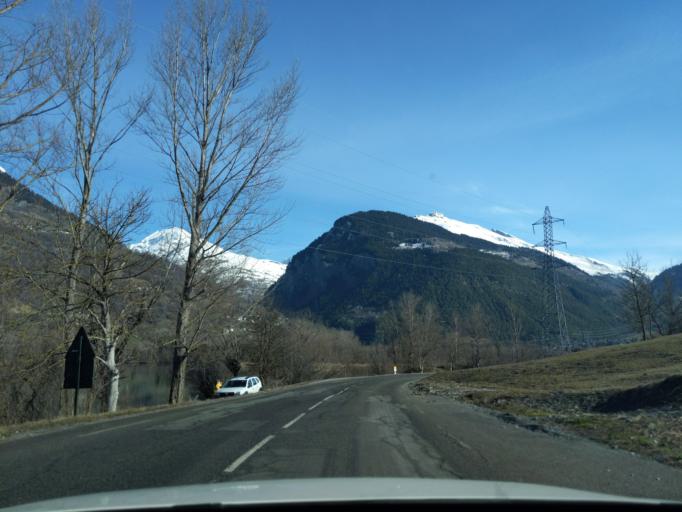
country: FR
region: Rhone-Alpes
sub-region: Departement de la Savoie
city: Bourg-Saint-Maurice
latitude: 45.6136
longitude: 6.7770
